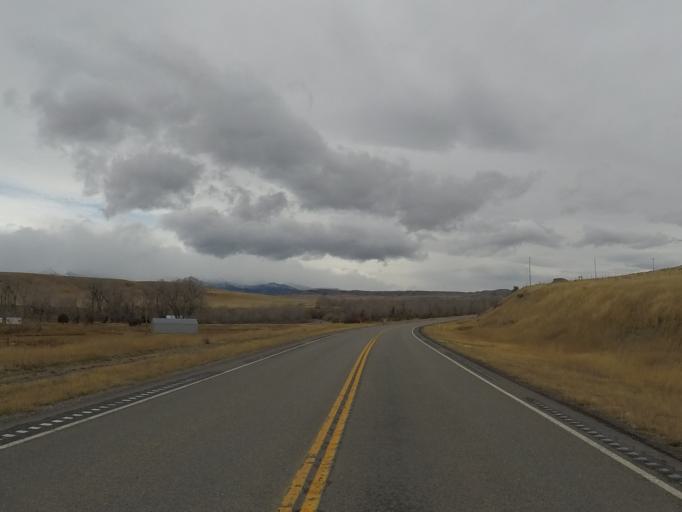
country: US
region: Montana
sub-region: Sweet Grass County
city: Big Timber
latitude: 45.9272
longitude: -109.9836
